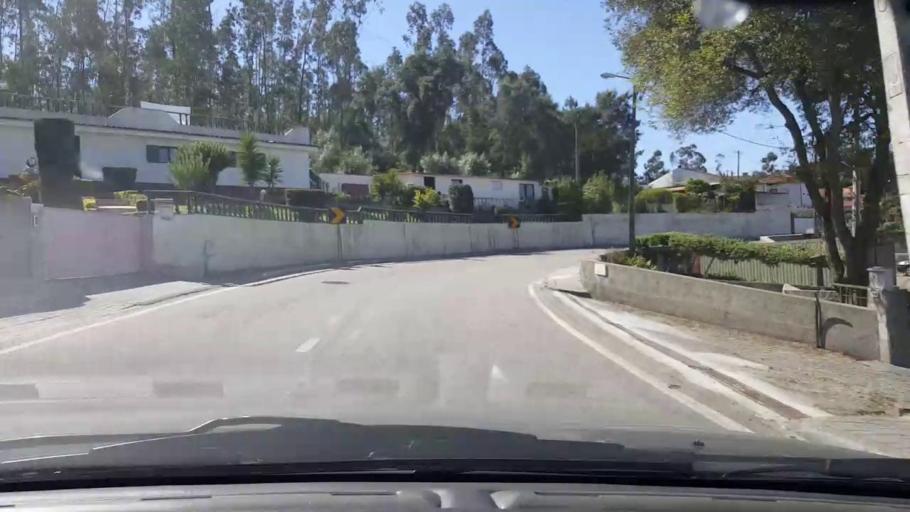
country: PT
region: Porto
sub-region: Vila do Conde
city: Arvore
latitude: 41.3415
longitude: -8.6592
